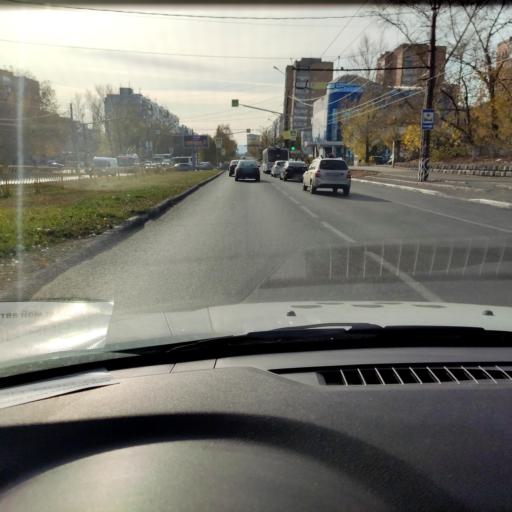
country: RU
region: Samara
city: Zhigulevsk
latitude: 53.4826
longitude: 49.4738
